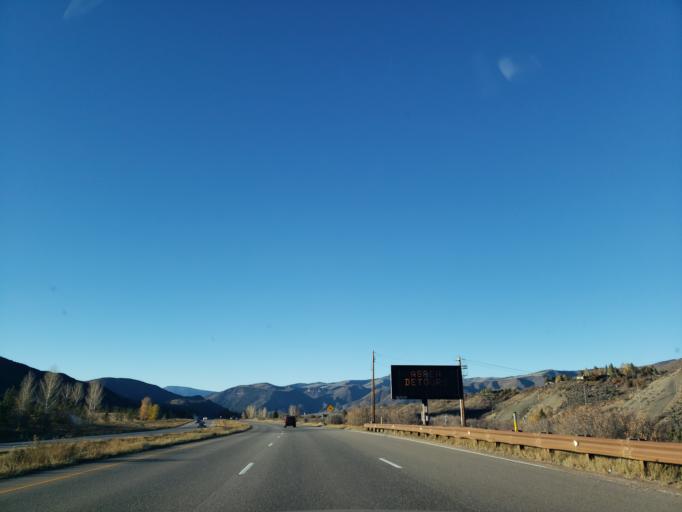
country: US
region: Colorado
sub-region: Pitkin County
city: Aspen
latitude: 39.2276
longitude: -106.8674
